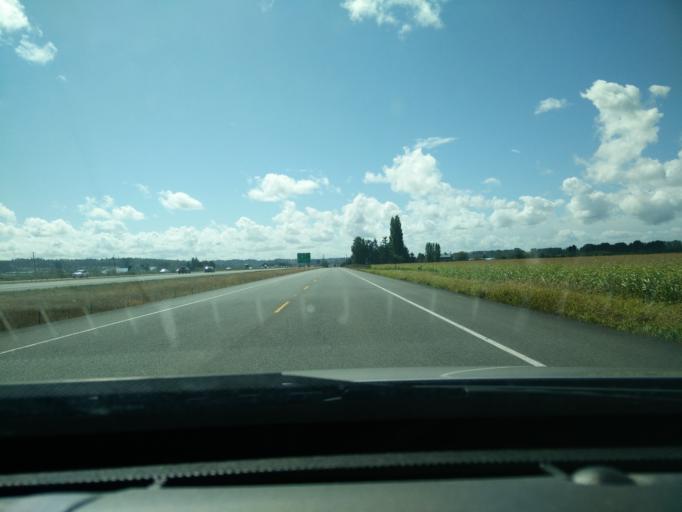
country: US
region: Washington
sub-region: Skagit County
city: Mount Vernon
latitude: 48.3620
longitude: -122.3365
